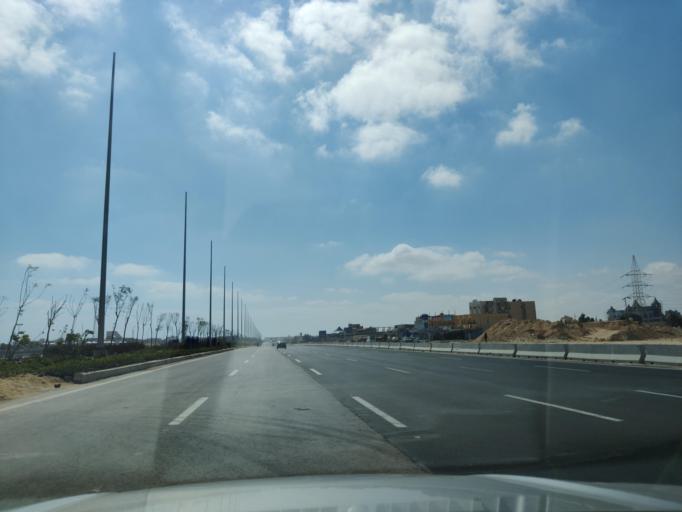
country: EG
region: Muhafazat Matruh
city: Al `Alamayn
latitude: 30.9918
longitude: 28.6753
